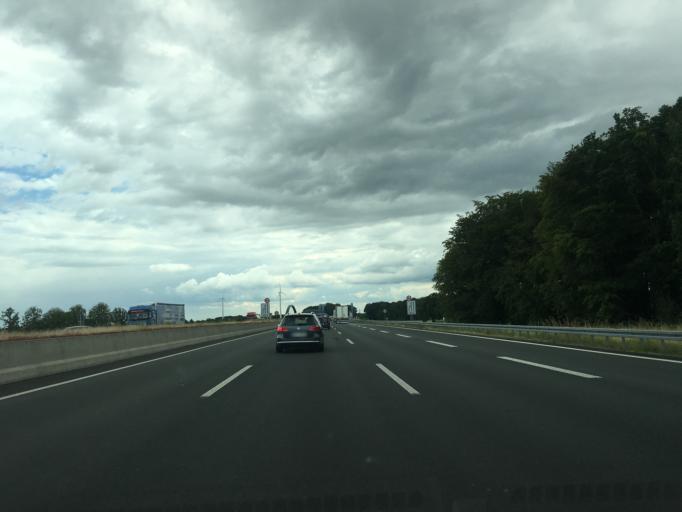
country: DE
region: North Rhine-Westphalia
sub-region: Regierungsbezirk Munster
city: Senden
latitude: 51.8830
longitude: 7.5755
